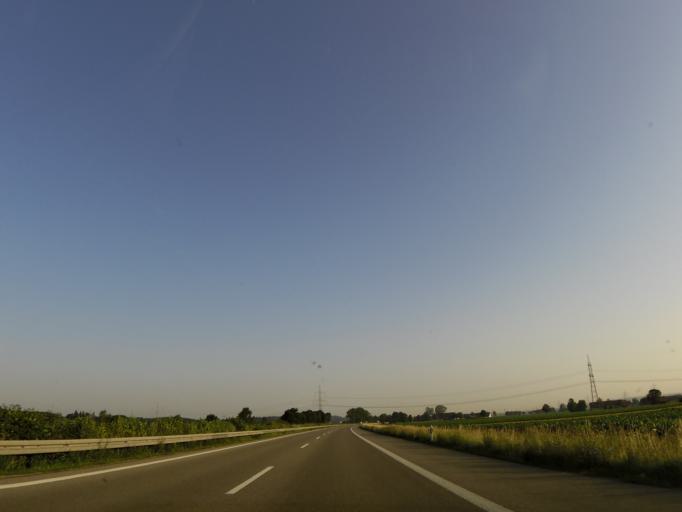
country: DE
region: Bavaria
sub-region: Swabia
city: Woringen
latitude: 47.9322
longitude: 10.2057
